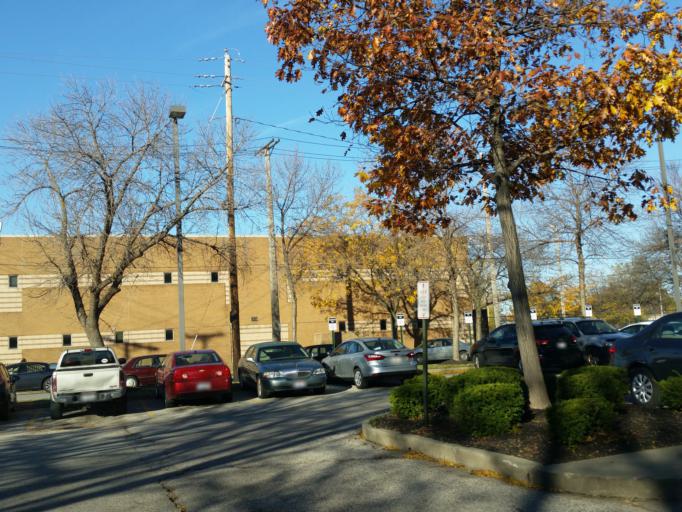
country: US
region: Ohio
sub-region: Cuyahoga County
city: Newburgh Heights
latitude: 41.4883
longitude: -81.6488
